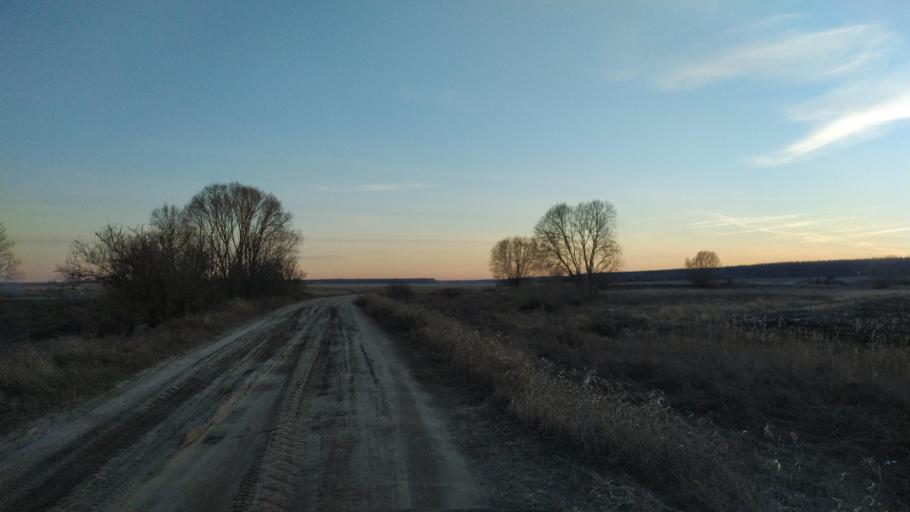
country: BY
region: Brest
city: Pruzhany
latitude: 52.5491
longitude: 24.2497
